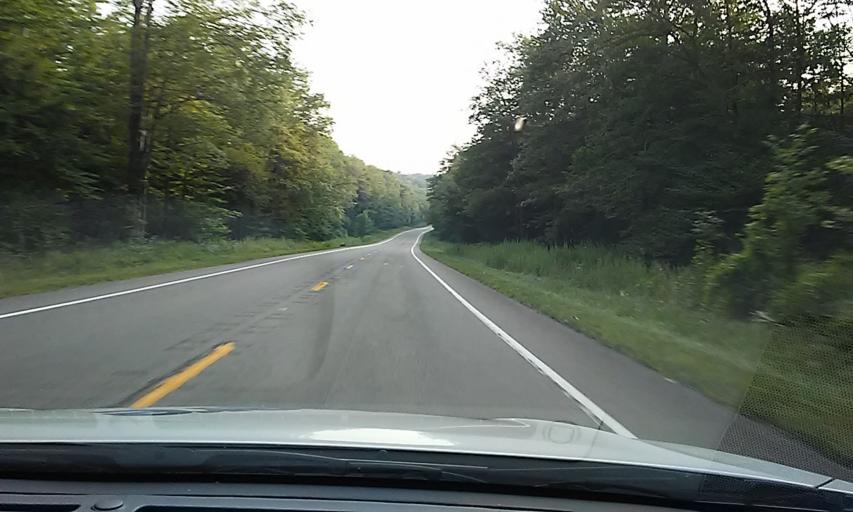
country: US
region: Pennsylvania
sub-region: Warren County
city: Sheffield
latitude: 41.5589
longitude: -78.9963
